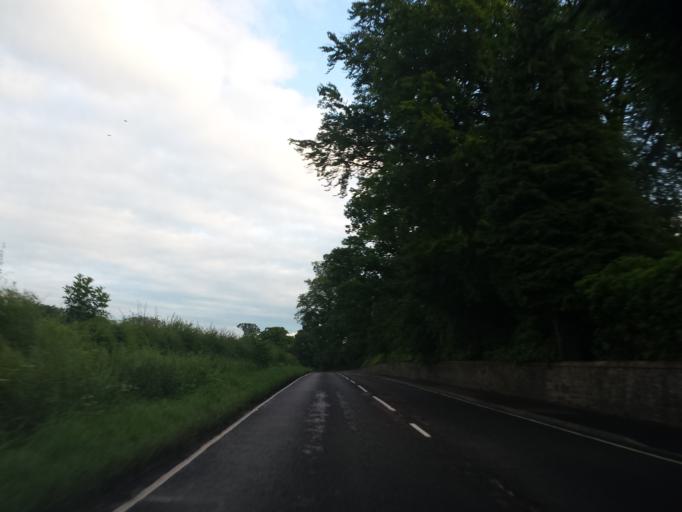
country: GB
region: Scotland
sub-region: Perth and Kinross
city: Scone
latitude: 56.4188
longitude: -3.4271
